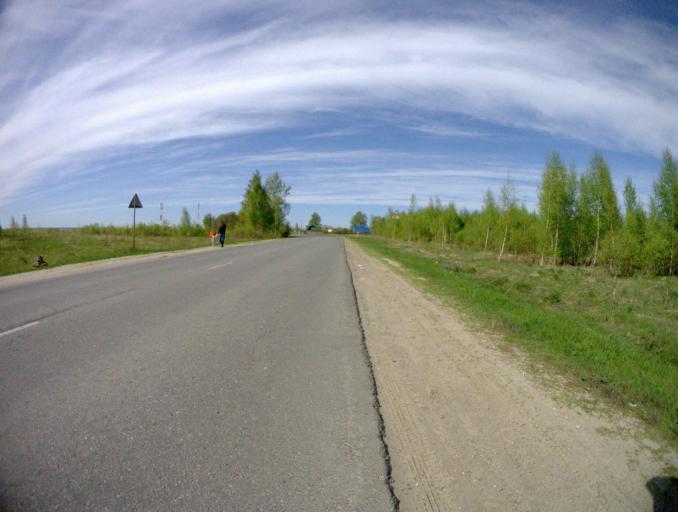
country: RU
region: Vladimir
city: Orgtrud
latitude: 56.2031
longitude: 40.5873
